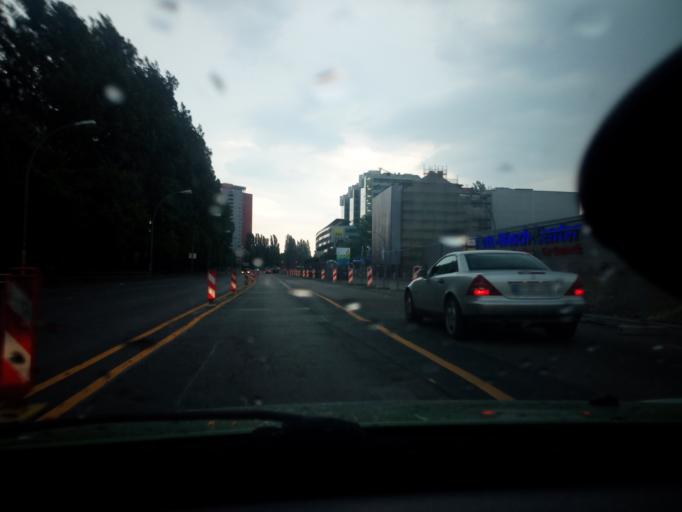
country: DE
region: Berlin
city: Berlin
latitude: 52.5152
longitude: 13.4196
